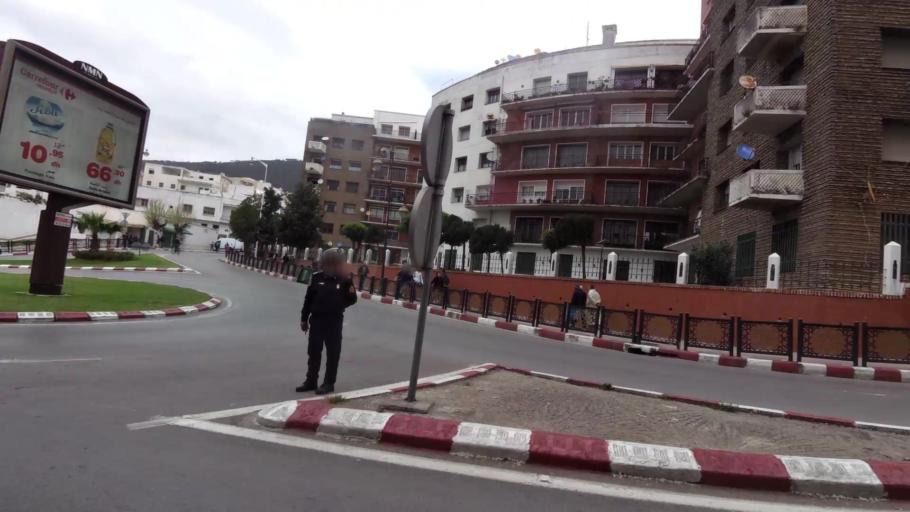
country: MA
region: Tanger-Tetouan
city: Tetouan
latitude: 35.5729
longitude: -5.3793
